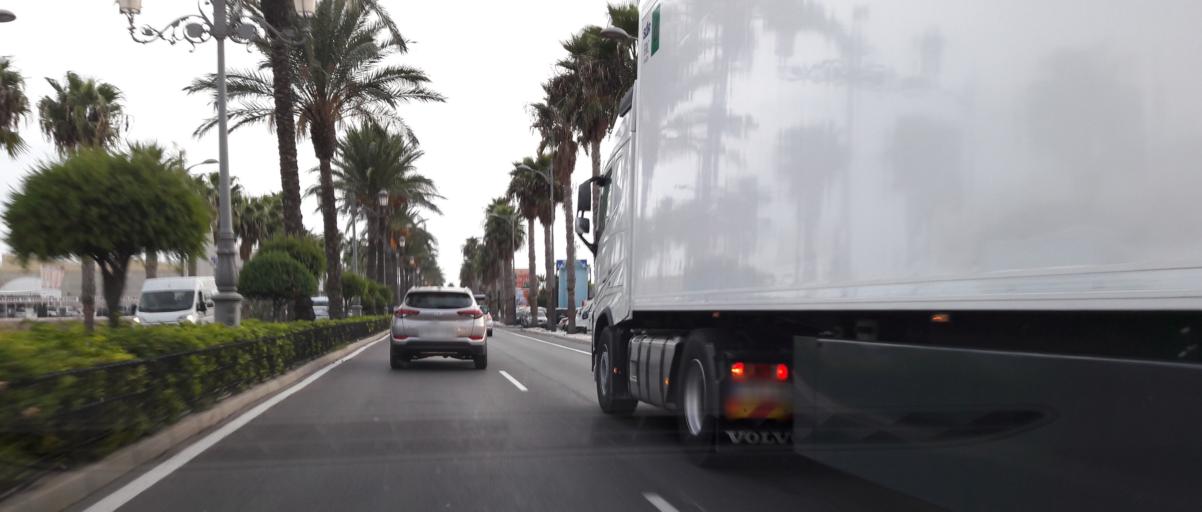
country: ES
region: Andalusia
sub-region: Provincia de Almeria
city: Roquetas de Mar
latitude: 36.7894
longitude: -2.6055
